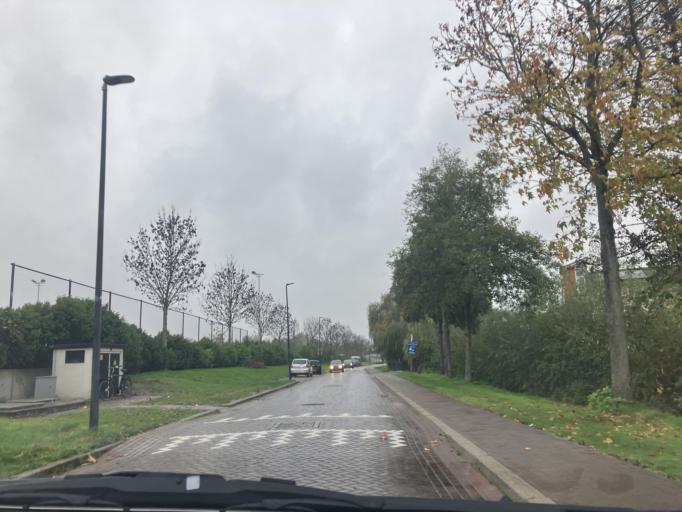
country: NL
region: South Holland
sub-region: Gemeente Rotterdam
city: Rotterdam
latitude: 51.9490
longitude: 4.5050
